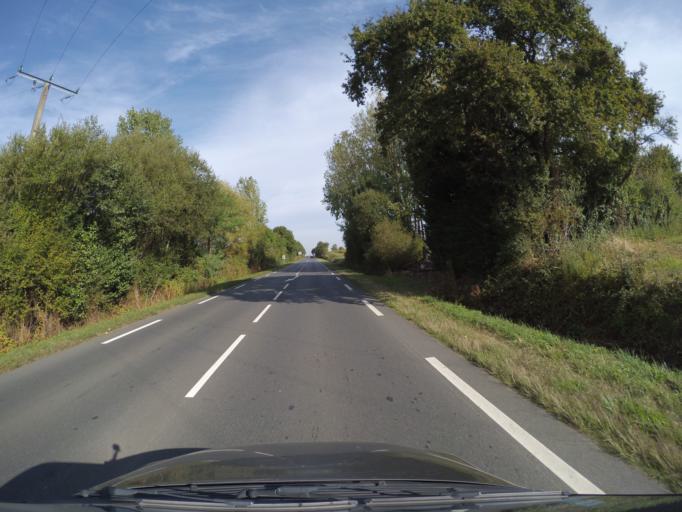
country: FR
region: Pays de la Loire
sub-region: Departement de la Loire-Atlantique
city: Gorges
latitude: 47.1158
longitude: -1.2827
